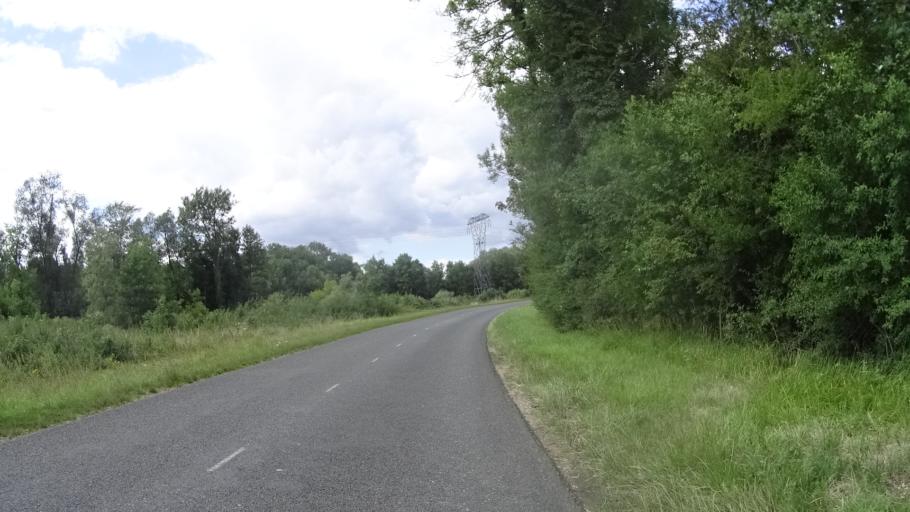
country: FR
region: Champagne-Ardenne
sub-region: Departement de la Haute-Marne
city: Villiers-en-Lieu
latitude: 48.6386
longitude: 4.8380
